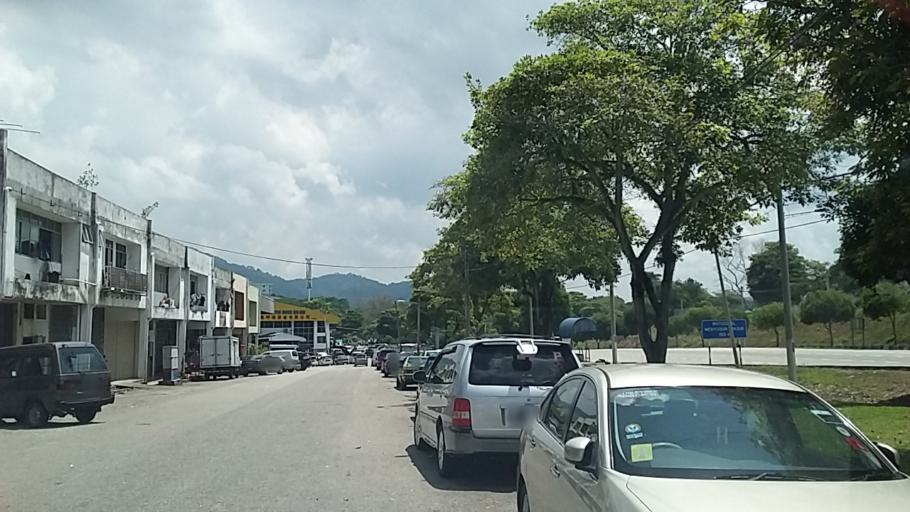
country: MY
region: Johor
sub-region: Daerah Batu Pahat
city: Batu Pahat
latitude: 1.7871
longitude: 102.9690
